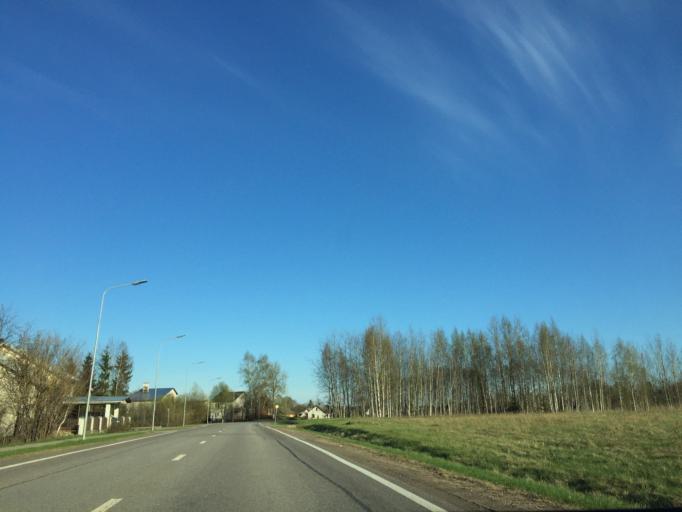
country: LV
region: Valkas Rajons
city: Valka
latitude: 57.7729
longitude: 25.9960
